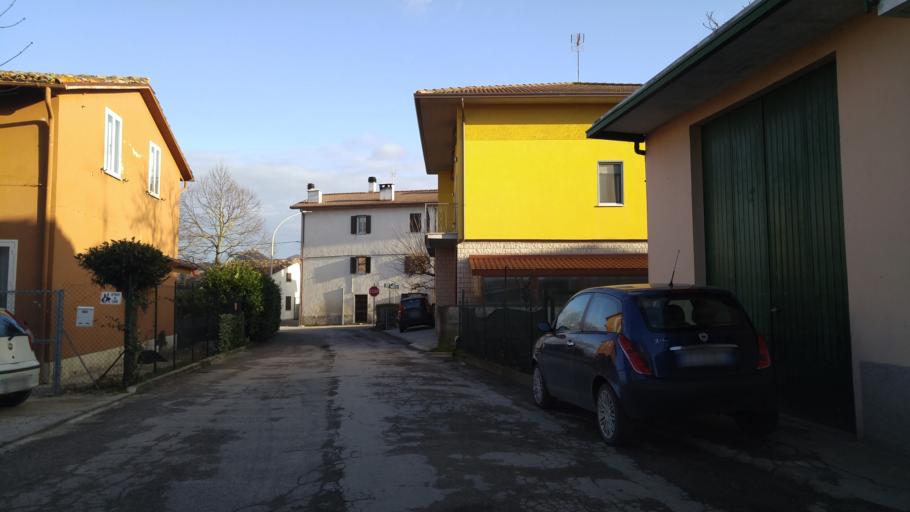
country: IT
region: The Marches
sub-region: Provincia di Pesaro e Urbino
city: Cagli
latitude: 43.5311
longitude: 12.6890
